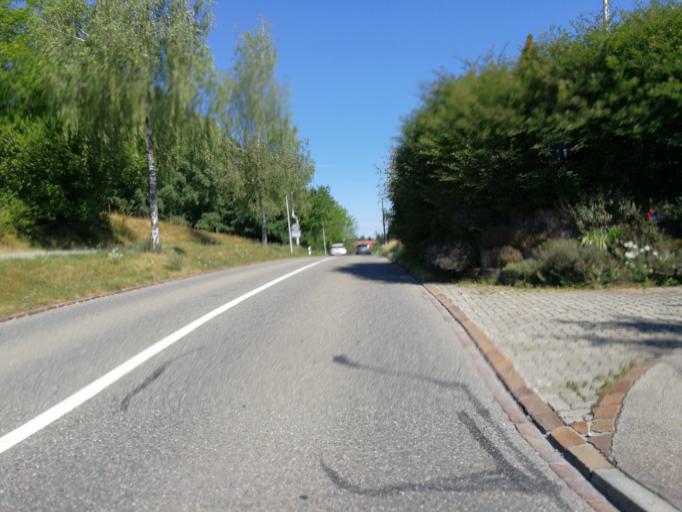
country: CH
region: Zurich
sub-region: Bezirk Uster
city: Uster / Nossikon
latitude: 47.3289
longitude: 8.7447
